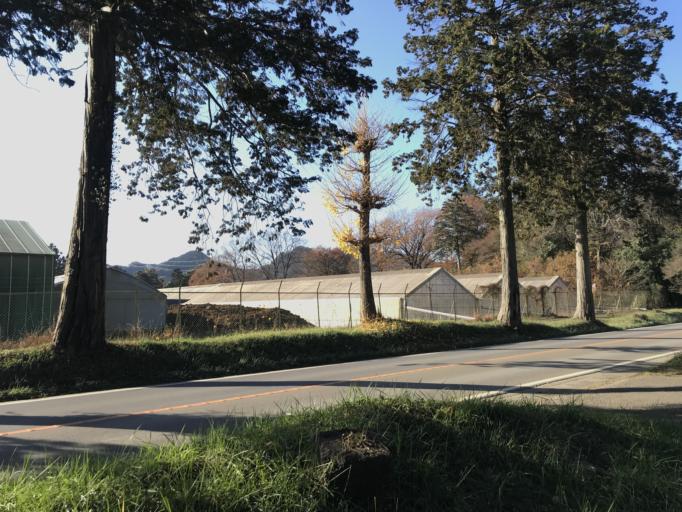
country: JP
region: Tochigi
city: Kanuma
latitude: 36.6092
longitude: 139.7407
